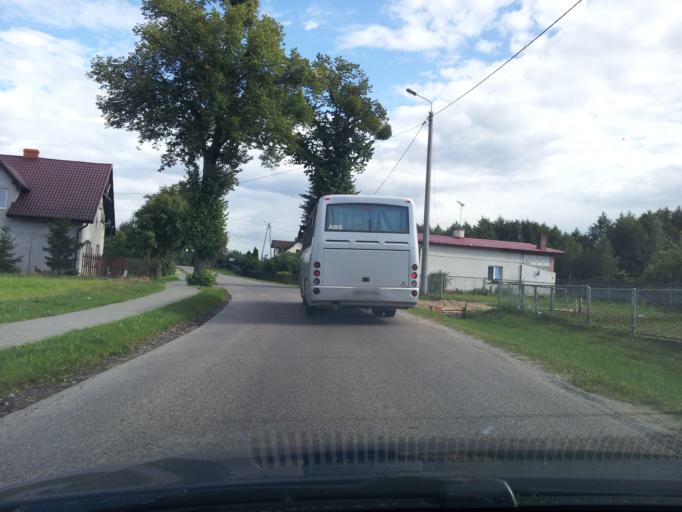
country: PL
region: Kujawsko-Pomorskie
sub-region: Powiat brodnicki
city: Bartniczka
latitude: 53.2413
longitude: 19.6144
